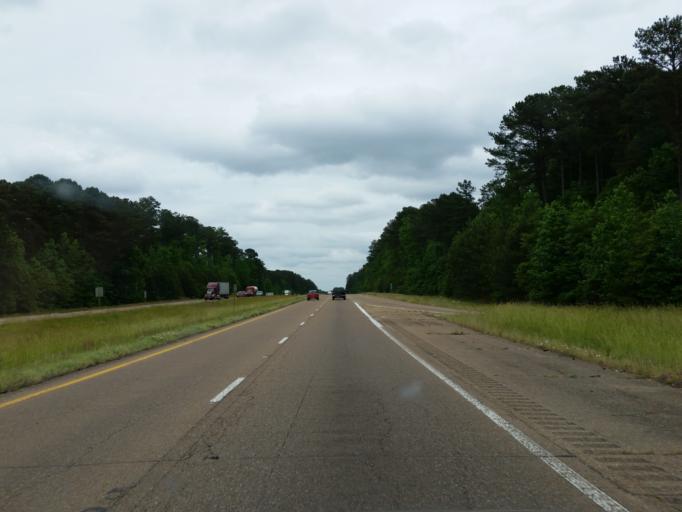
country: US
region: Mississippi
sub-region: Lauderdale County
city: Marion
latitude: 32.3960
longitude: -88.5786
